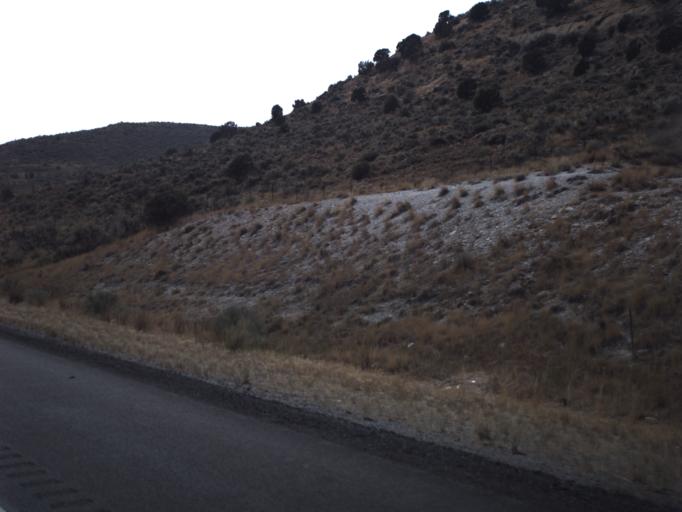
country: US
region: Wyoming
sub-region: Uinta County
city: Evanston
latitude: 41.1755
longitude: -111.1348
